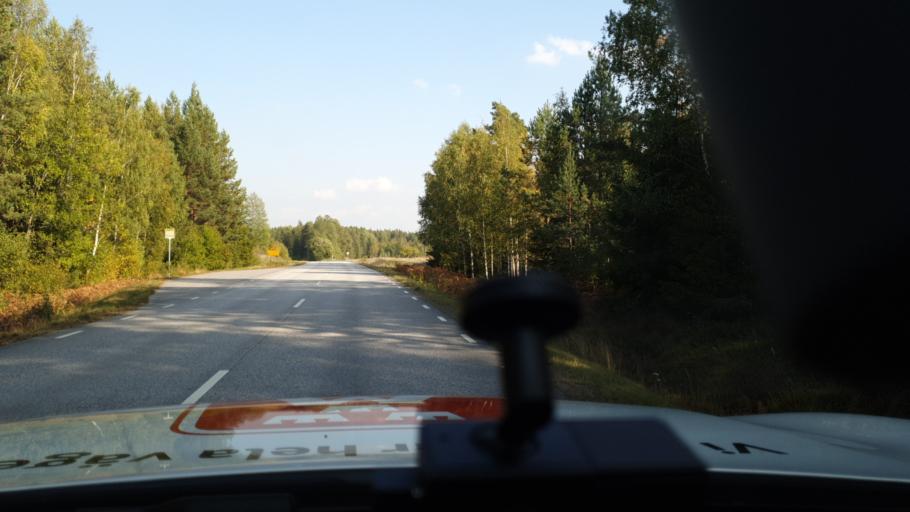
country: SE
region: Kalmar
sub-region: Vimmerby Kommun
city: Vimmerby
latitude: 57.5872
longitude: 15.9930
